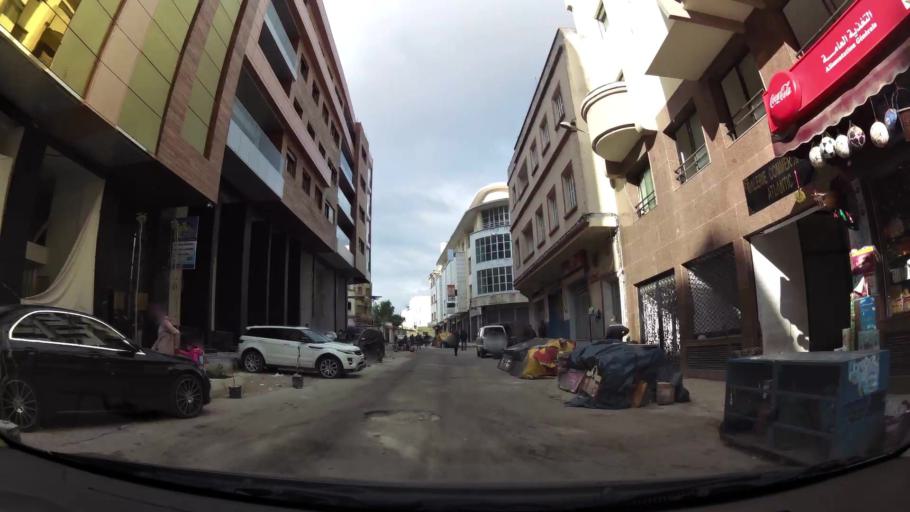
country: MA
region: Tanger-Tetouan
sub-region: Tanger-Assilah
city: Tangier
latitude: 35.7761
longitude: -5.8144
